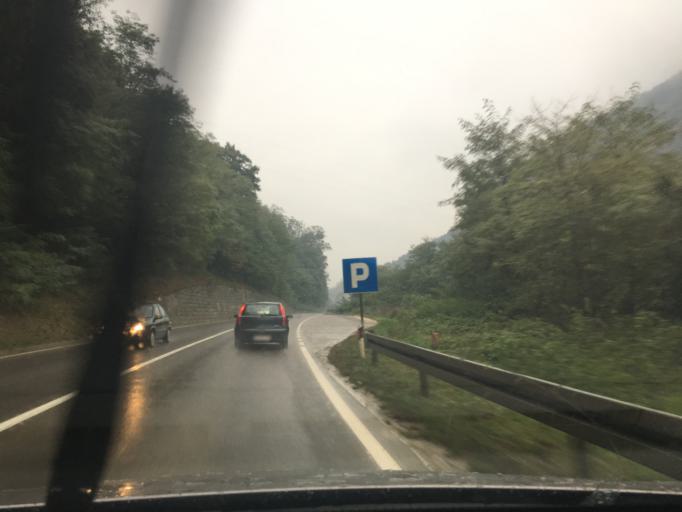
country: RS
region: Central Serbia
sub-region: Pcinjski Okrug
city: Vladicin Han
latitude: 42.7561
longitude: 22.0823
